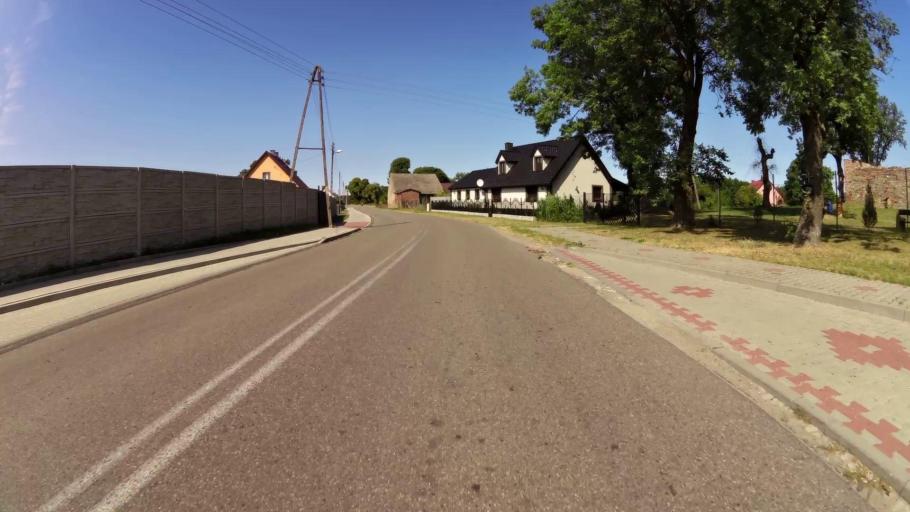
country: PL
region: West Pomeranian Voivodeship
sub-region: Powiat stargardzki
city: Dobrzany
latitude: 53.3417
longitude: 15.3956
